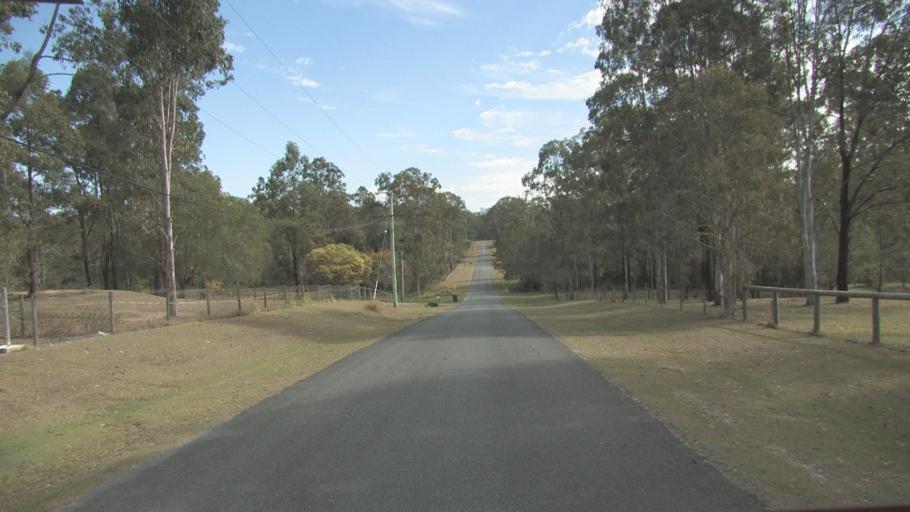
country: AU
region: Queensland
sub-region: Logan
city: North Maclean
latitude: -27.7661
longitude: 152.9896
